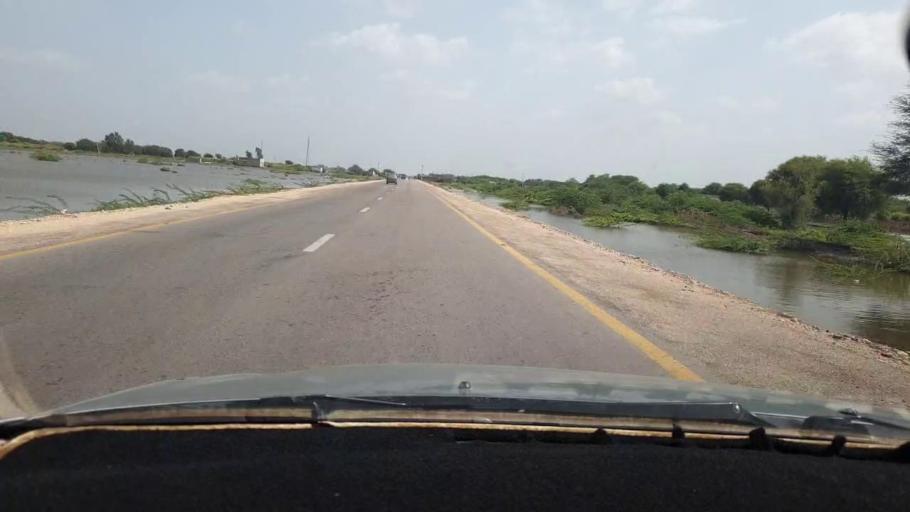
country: PK
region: Sindh
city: Digri
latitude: 25.1220
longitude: 69.1488
